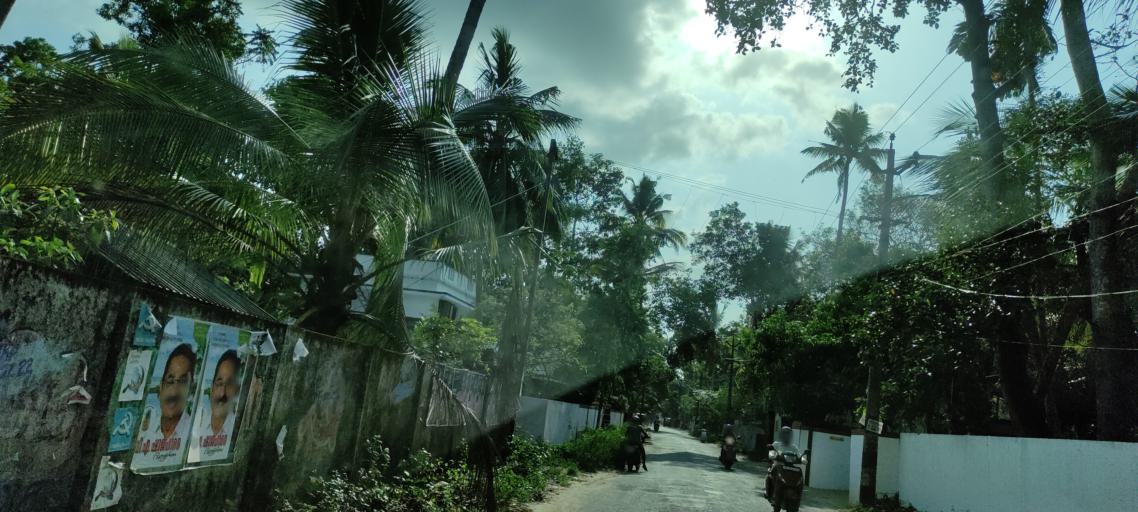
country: IN
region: Kerala
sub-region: Alappuzha
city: Vayalar
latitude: 9.6876
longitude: 76.3163
